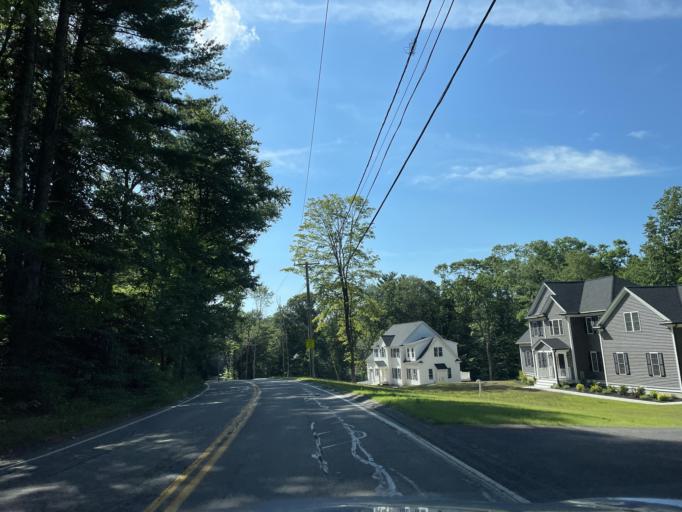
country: US
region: Massachusetts
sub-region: Worcester County
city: Mendon
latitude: 42.1203
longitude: -71.5898
